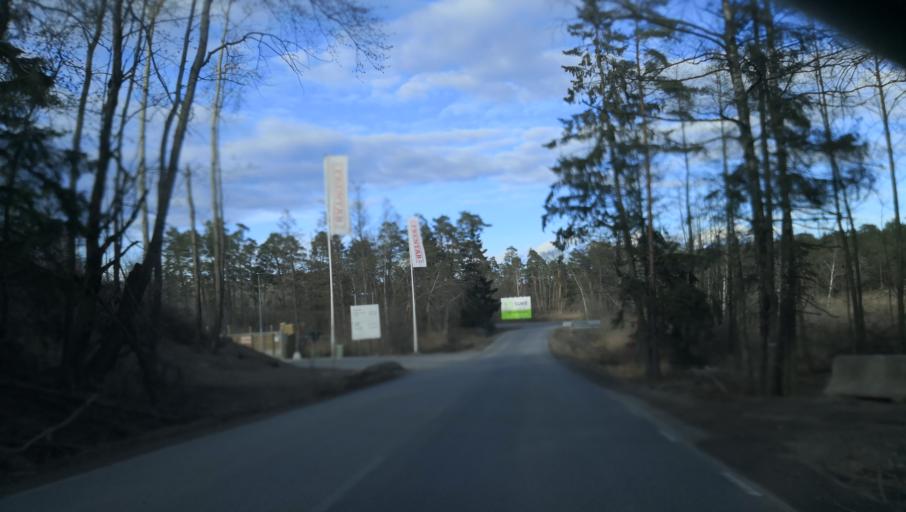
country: SE
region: Stockholm
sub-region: Varmdo Kommun
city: Gustavsberg
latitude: 59.3446
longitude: 18.3563
